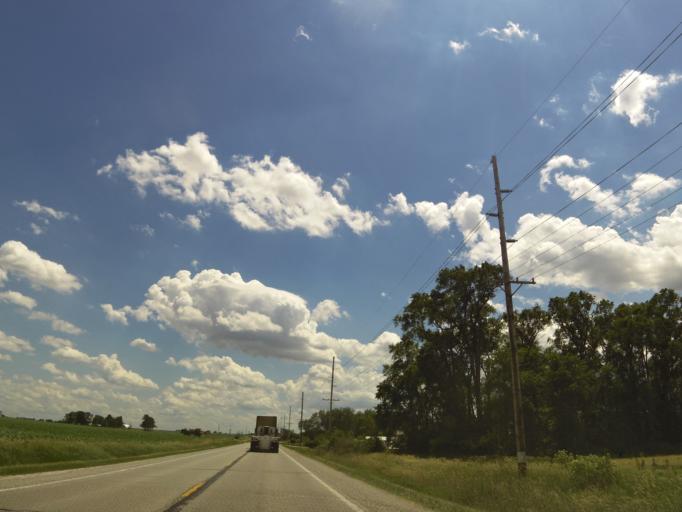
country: US
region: Iowa
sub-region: Buchanan County
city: Independence
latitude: 42.3775
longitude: -91.8894
